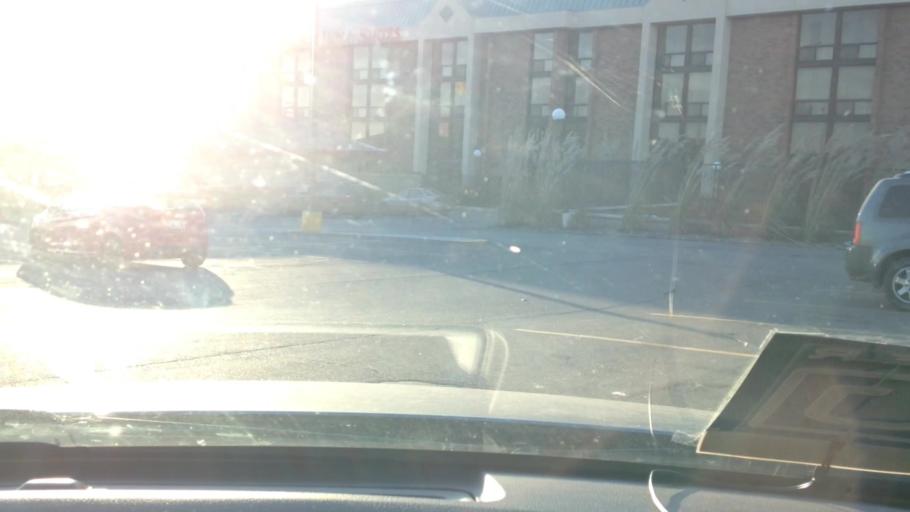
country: US
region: Missouri
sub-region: Jackson County
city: Raytown
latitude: 39.0536
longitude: -94.4735
